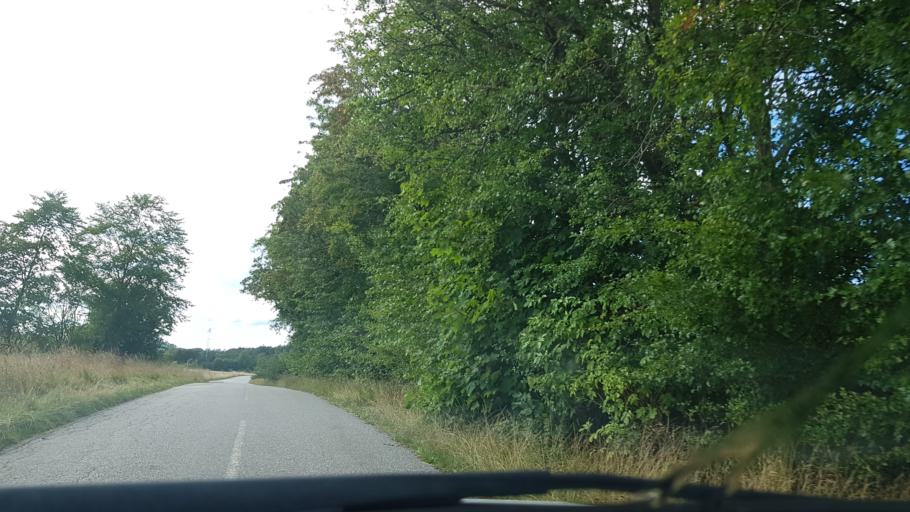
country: DK
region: Capital Region
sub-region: Fredensborg Kommune
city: Humlebaek
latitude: 55.9804
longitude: 12.4889
